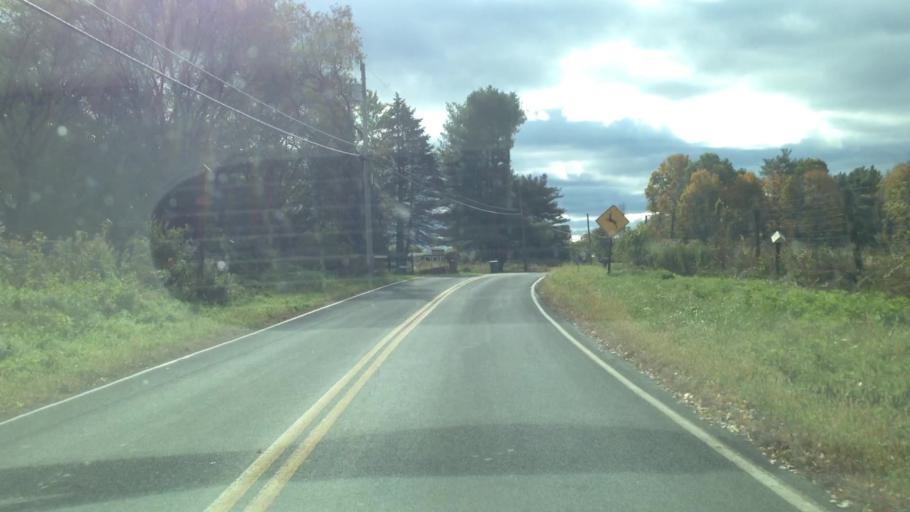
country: US
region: New York
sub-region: Ulster County
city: Tillson
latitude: 41.7928
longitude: -74.0876
